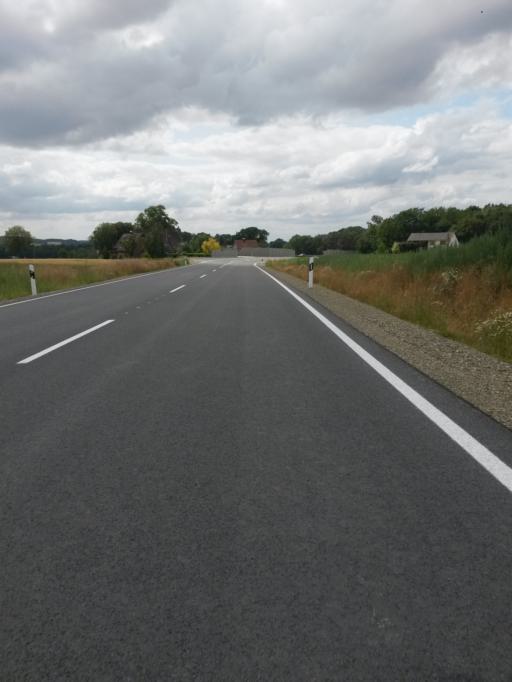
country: DE
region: North Rhine-Westphalia
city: Bad Oeynhausen
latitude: 52.1617
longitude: 8.7598
